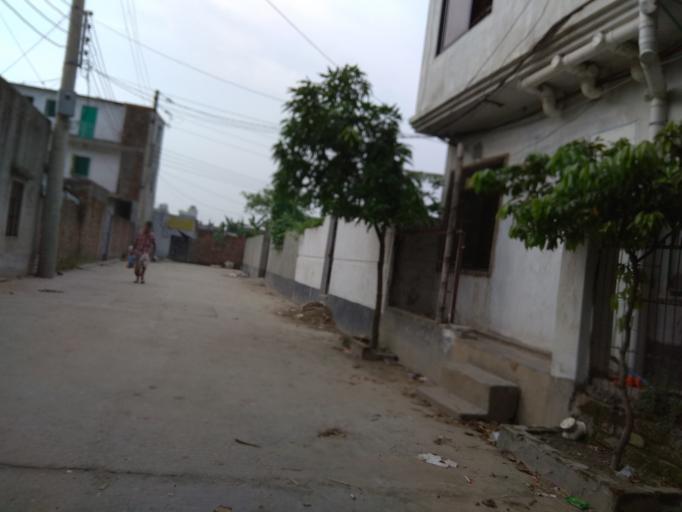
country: BD
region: Dhaka
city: Paltan
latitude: 23.8102
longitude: 90.3829
